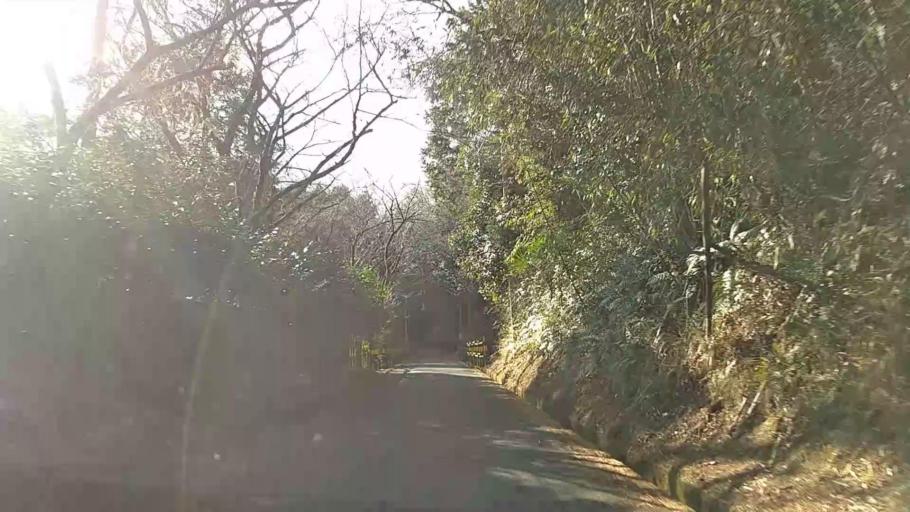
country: JP
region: Kanagawa
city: Isehara
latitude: 35.4467
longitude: 139.2864
